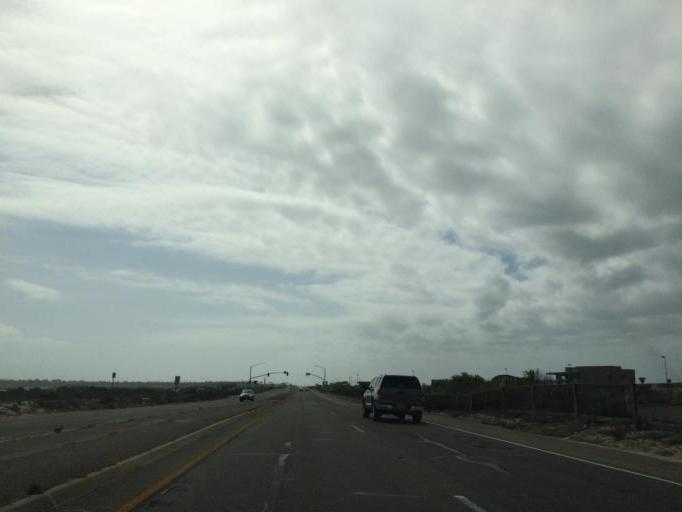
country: US
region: California
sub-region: Orange County
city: Huntington Beach
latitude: 33.6968
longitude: -118.0483
